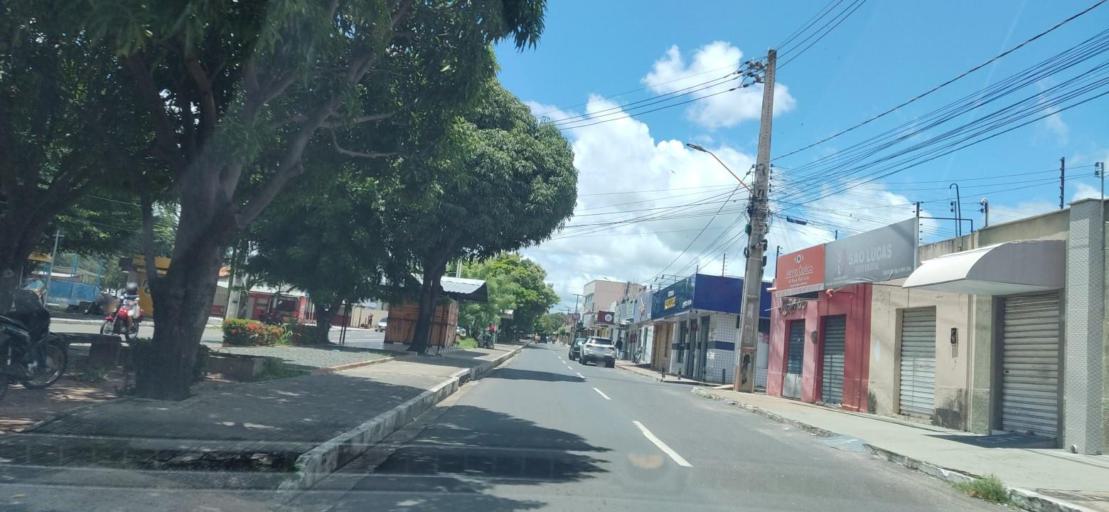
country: BR
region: Piaui
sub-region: Teresina
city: Teresina
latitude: -5.1495
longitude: -42.7833
